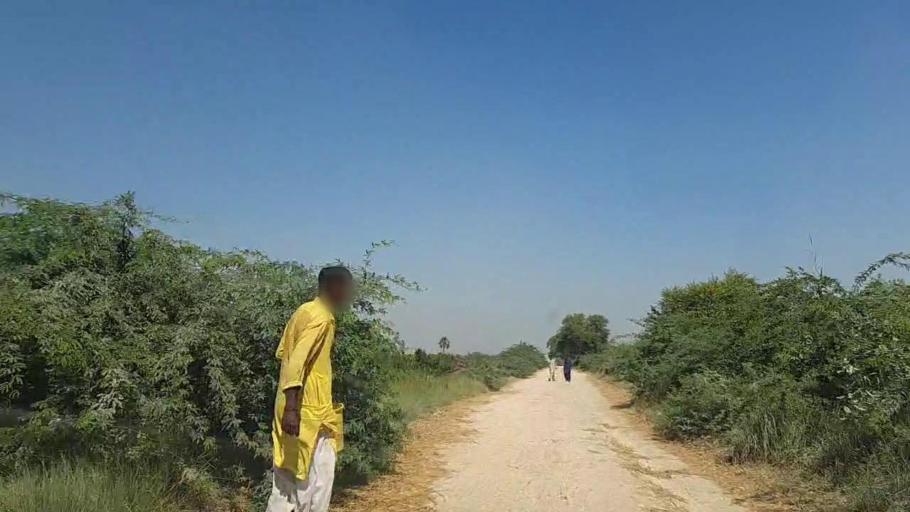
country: PK
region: Sindh
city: Daro Mehar
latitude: 24.8025
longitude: 68.1816
